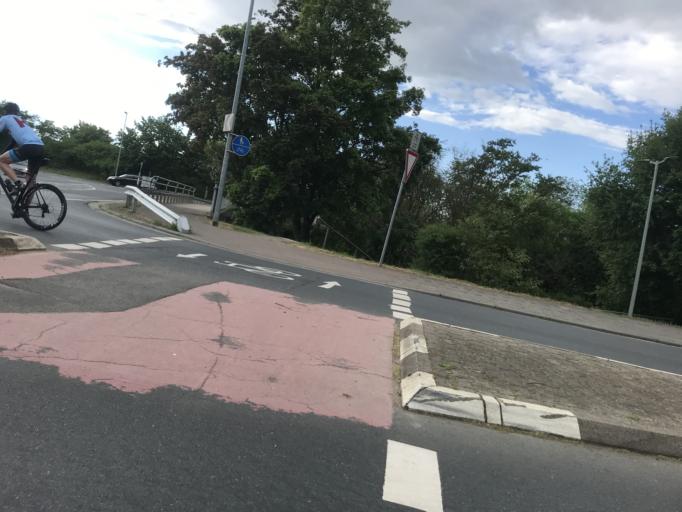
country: DE
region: Rheinland-Pfalz
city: Nieder-Olm
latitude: 49.8996
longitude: 8.2013
